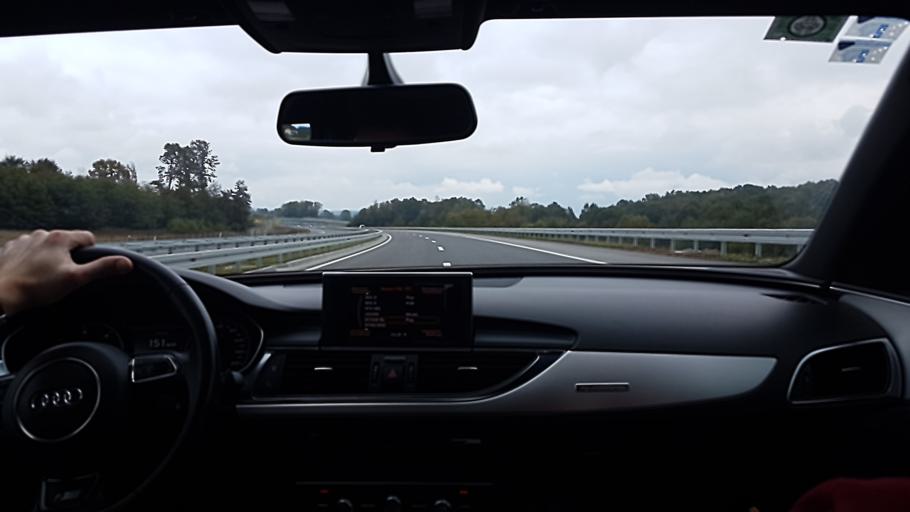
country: BA
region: Republika Srpska
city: Prnjavor
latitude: 44.8475
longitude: 17.7530
